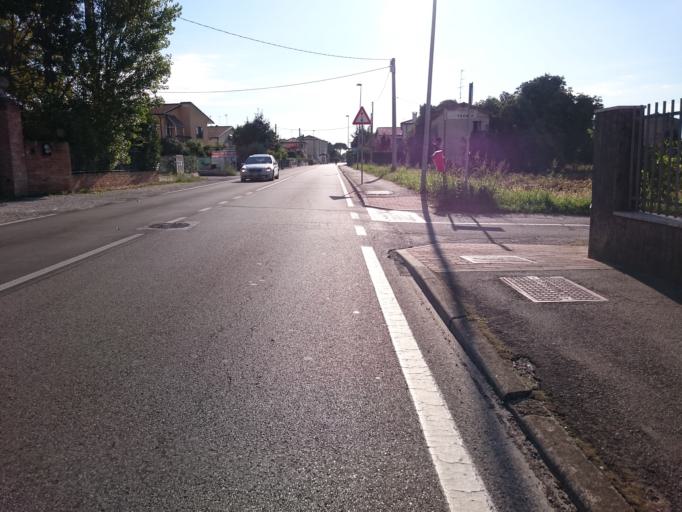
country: IT
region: Veneto
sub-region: Provincia di Padova
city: Albignasego
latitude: 45.3393
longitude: 11.8881
